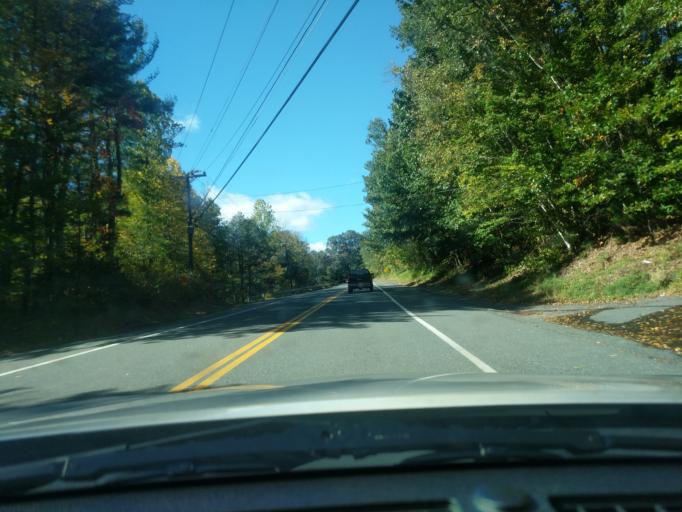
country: US
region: Massachusetts
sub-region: Hampden County
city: Granville
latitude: 42.1637
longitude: -72.8450
